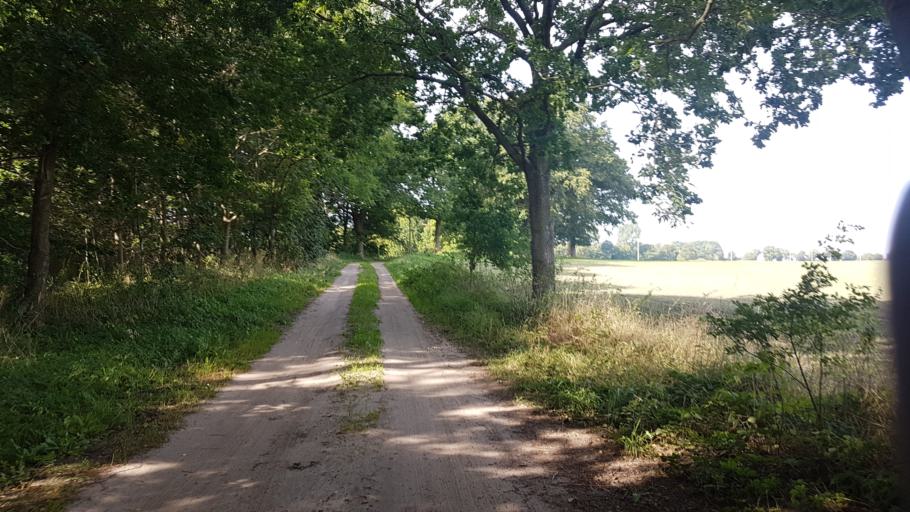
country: DE
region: Mecklenburg-Vorpommern
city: Samtens
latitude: 54.3899
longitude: 13.2646
